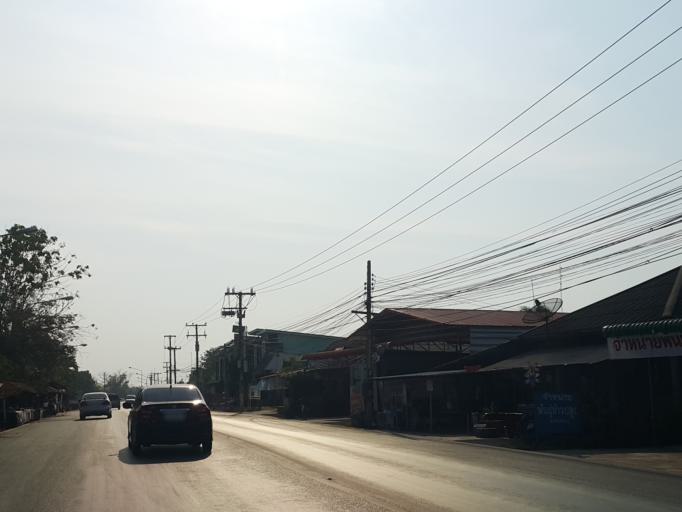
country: TH
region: Phitsanulok
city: Phrom Phiram
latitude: 16.9389
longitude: 100.2291
